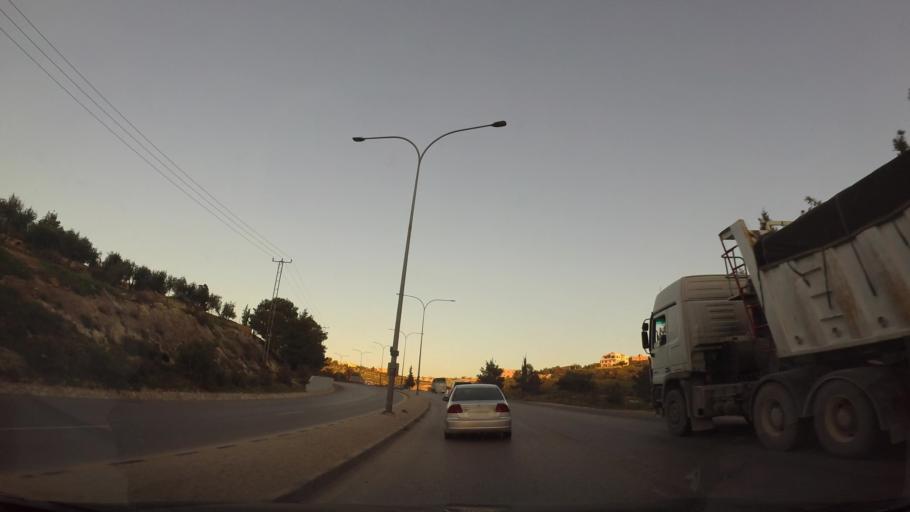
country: JO
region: Amman
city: Umm as Summaq
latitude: 31.8618
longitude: 35.7943
